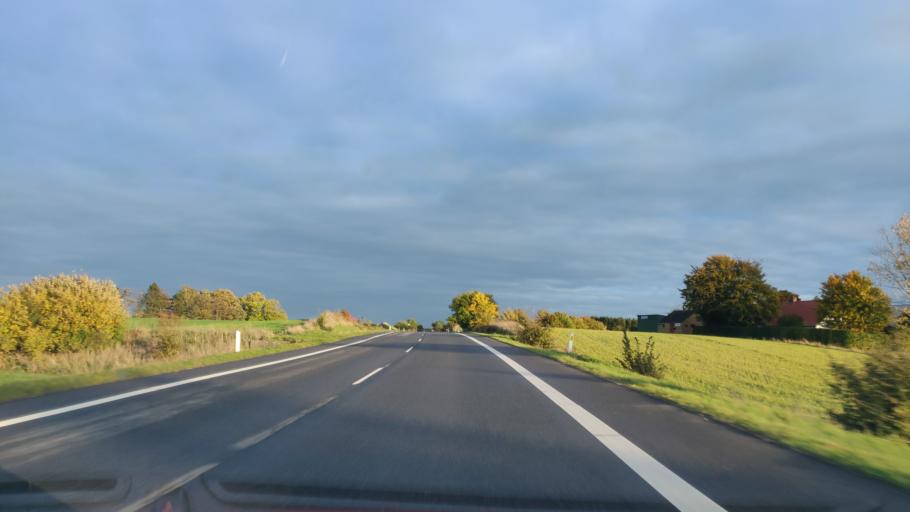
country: DK
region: Zealand
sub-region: Holbaek Kommune
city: Holbaek
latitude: 55.6853
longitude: 11.7051
